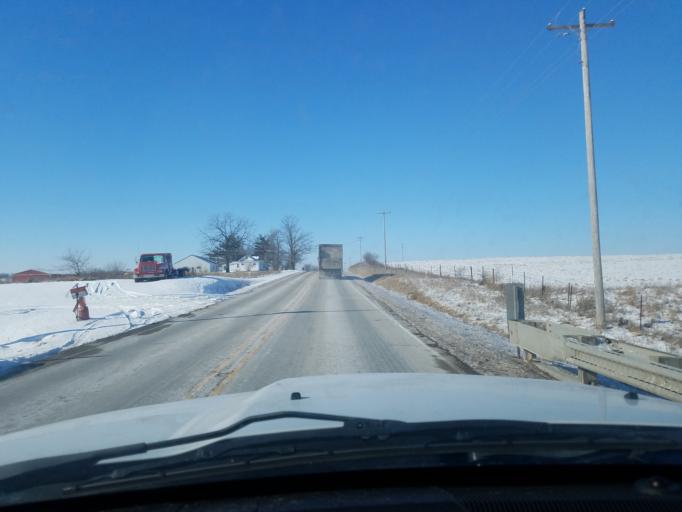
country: US
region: Indiana
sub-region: Noble County
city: Kendallville
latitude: 41.3947
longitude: -85.3027
